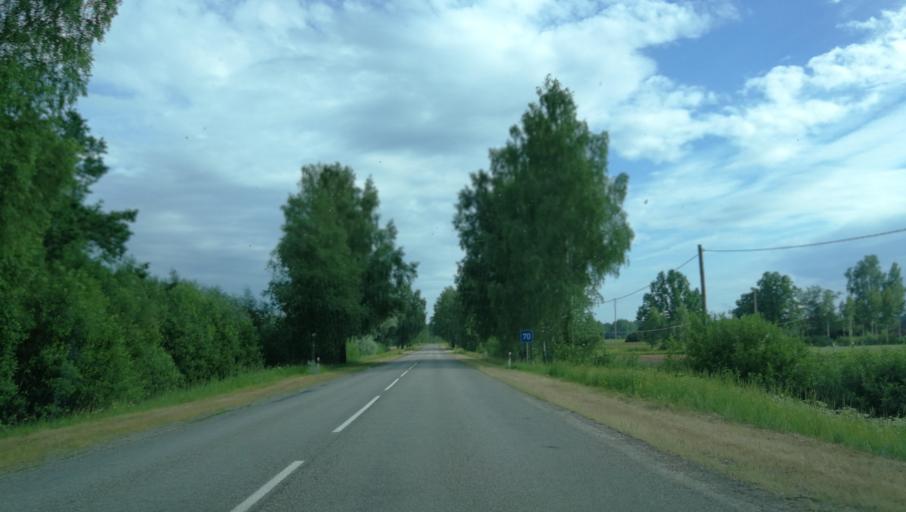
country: LV
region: Valmieras Rajons
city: Valmiera
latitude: 57.5929
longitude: 25.4607
